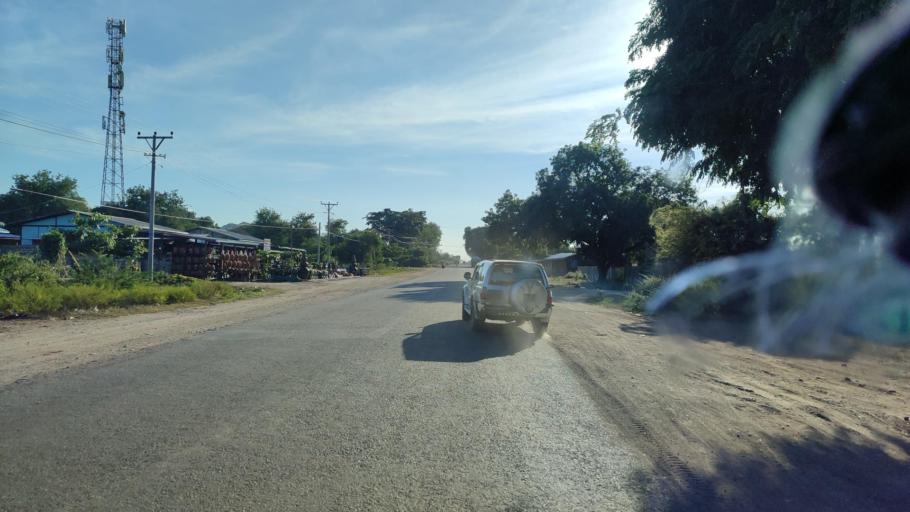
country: MM
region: Mandalay
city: Yamethin
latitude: 20.7438
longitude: 96.2150
